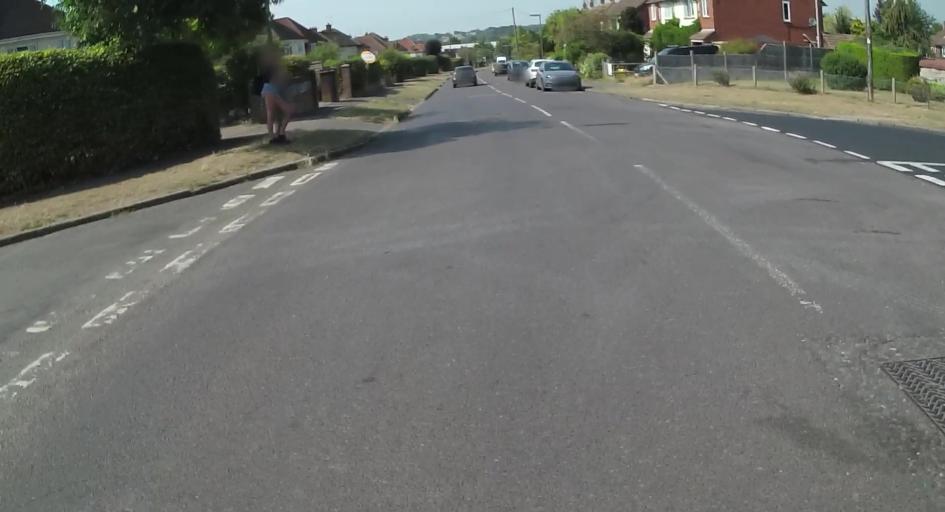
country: GB
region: England
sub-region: Surrey
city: Farnham
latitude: 51.2025
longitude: -0.8081
